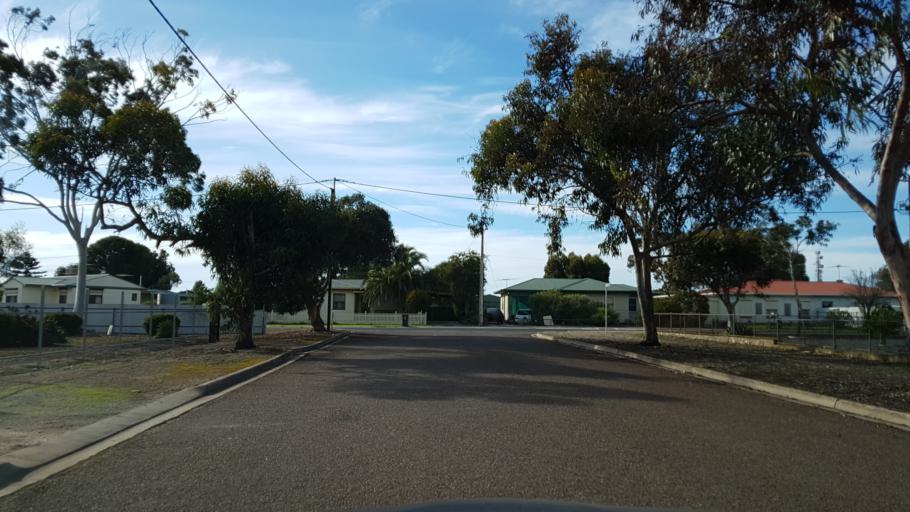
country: AU
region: South Australia
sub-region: Murray Bridge
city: Tailem Bend
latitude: -35.2526
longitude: 139.4621
